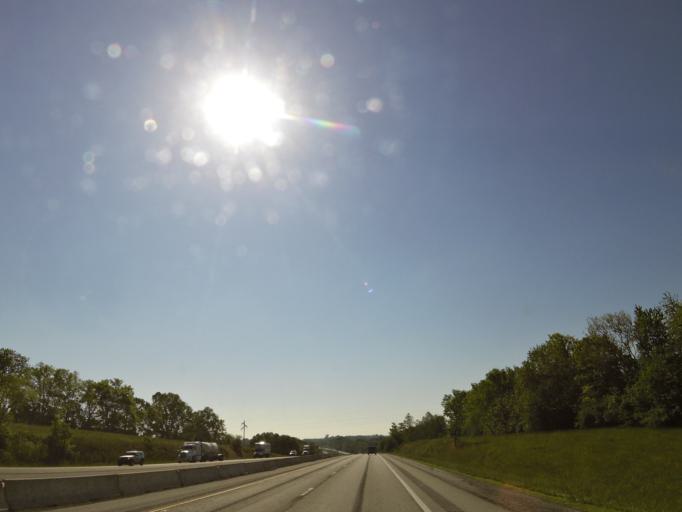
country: US
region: Kentucky
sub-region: Shelby County
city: Shelbyville
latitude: 38.1878
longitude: -85.2564
